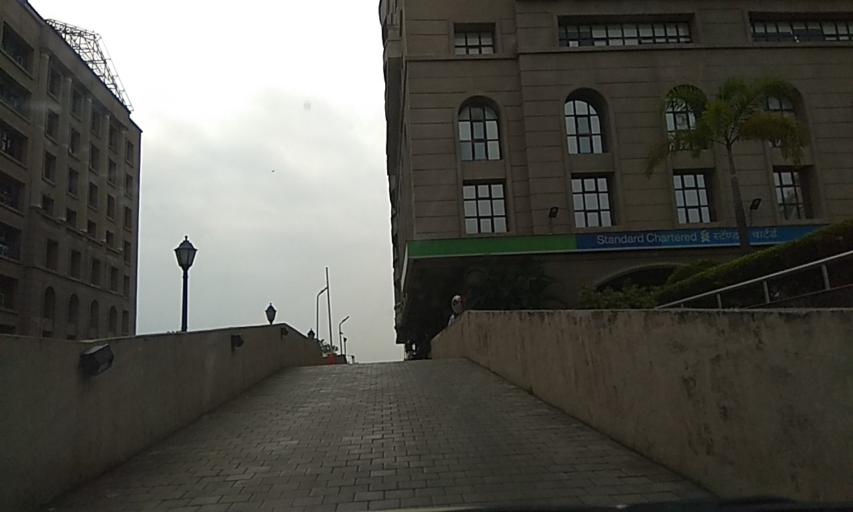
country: IN
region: Maharashtra
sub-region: Pune Division
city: Lohogaon
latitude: 18.5452
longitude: 73.9102
